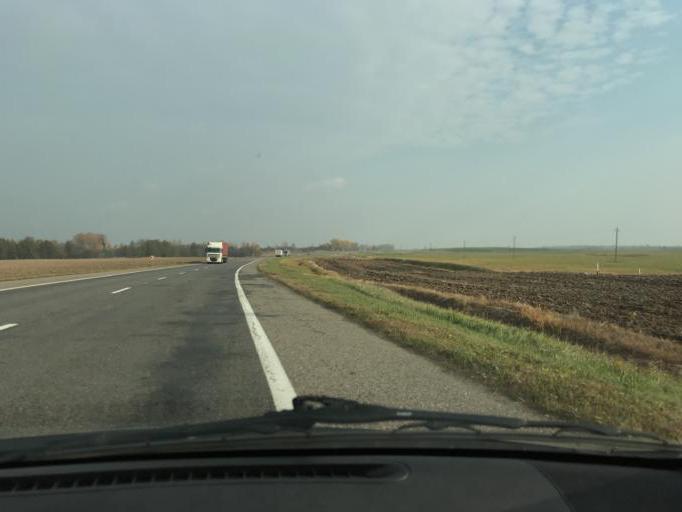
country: BY
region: Vitebsk
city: Chashniki
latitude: 55.0042
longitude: 28.9677
